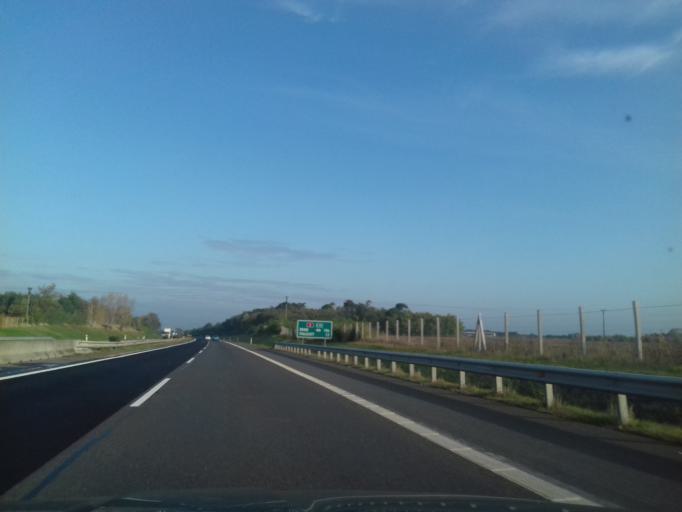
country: SK
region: Bratislavsky
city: Stupava
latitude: 48.3317
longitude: 17.0243
